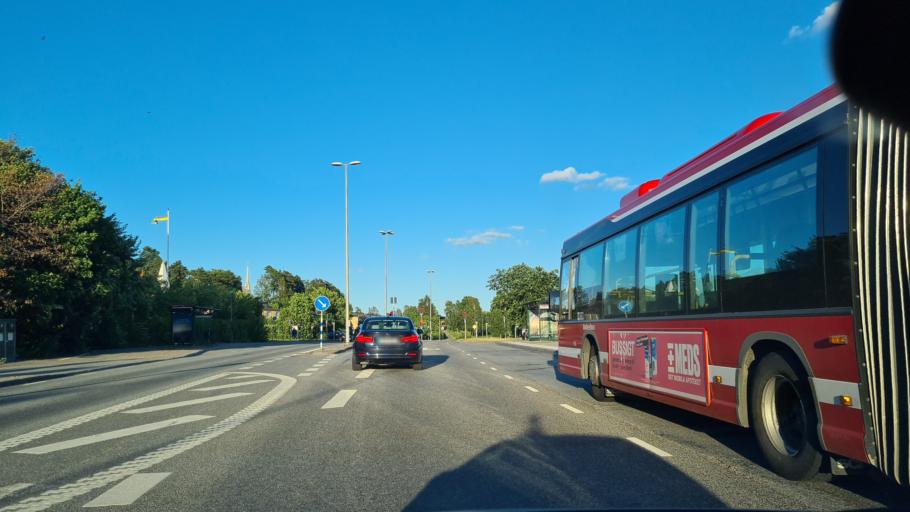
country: SE
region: Stockholm
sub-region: Sodertalje Kommun
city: Pershagen
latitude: 59.1851
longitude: 17.6601
